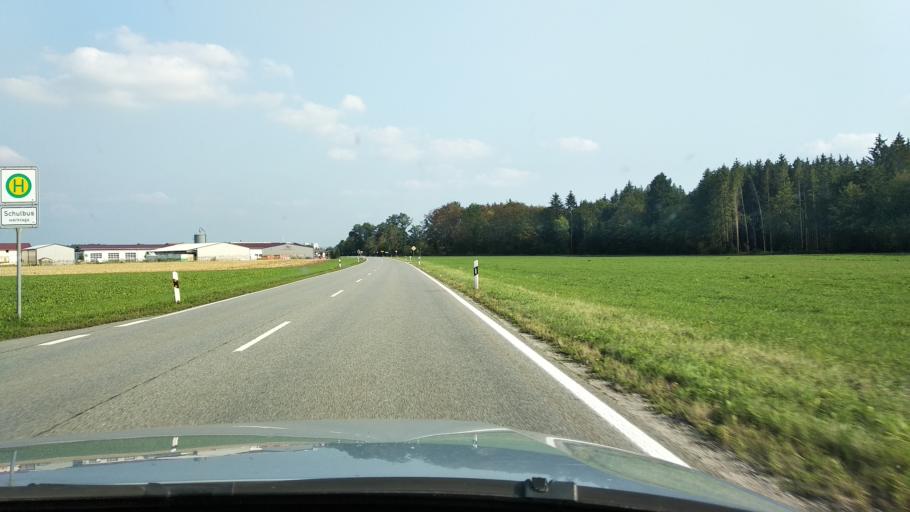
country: DE
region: Bavaria
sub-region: Upper Bavaria
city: Edling
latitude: 48.0707
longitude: 12.1444
